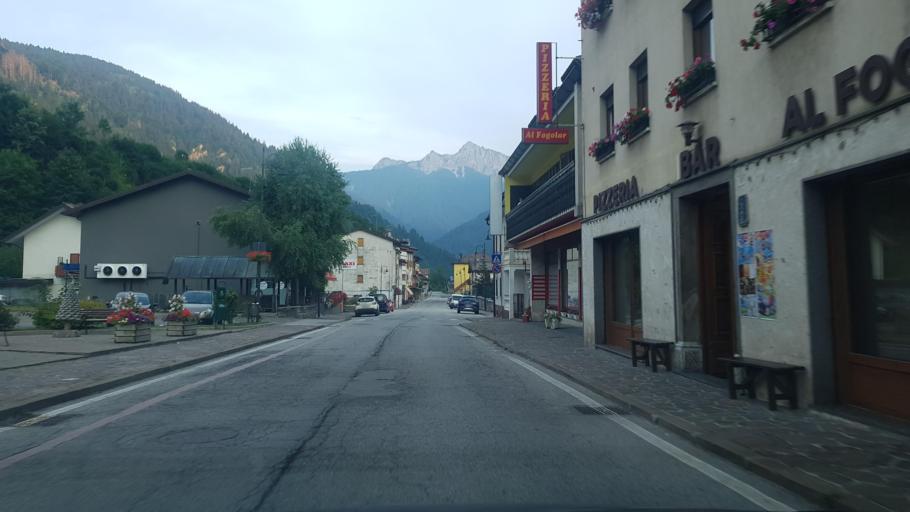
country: IT
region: Friuli Venezia Giulia
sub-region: Provincia di Udine
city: Paularo
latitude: 46.5294
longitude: 13.1176
